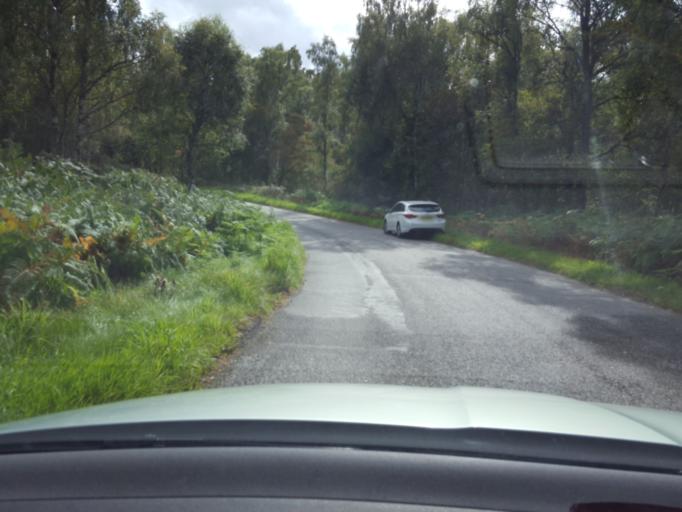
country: GB
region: Scotland
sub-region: Aberdeenshire
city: Ballater
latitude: 57.0843
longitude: -2.9435
